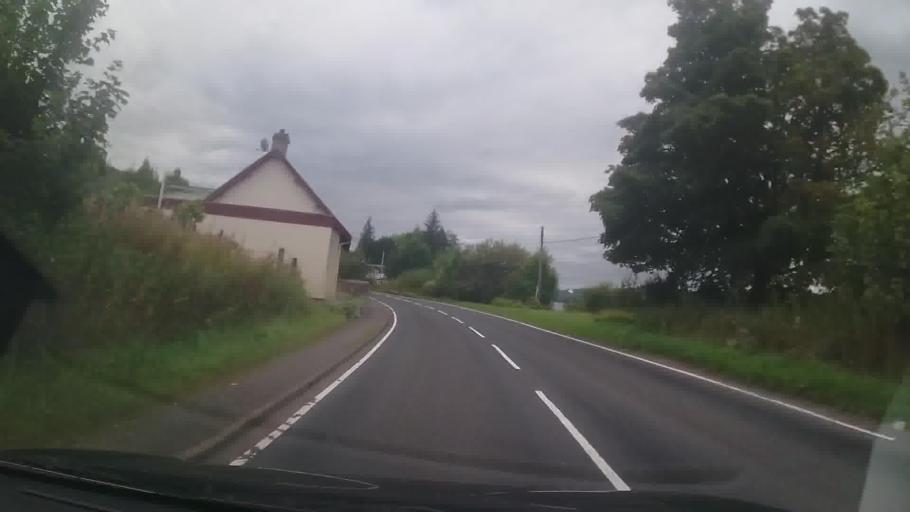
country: GB
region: Scotland
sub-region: Argyll and Bute
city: Garelochhead
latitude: 56.2228
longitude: -5.0320
